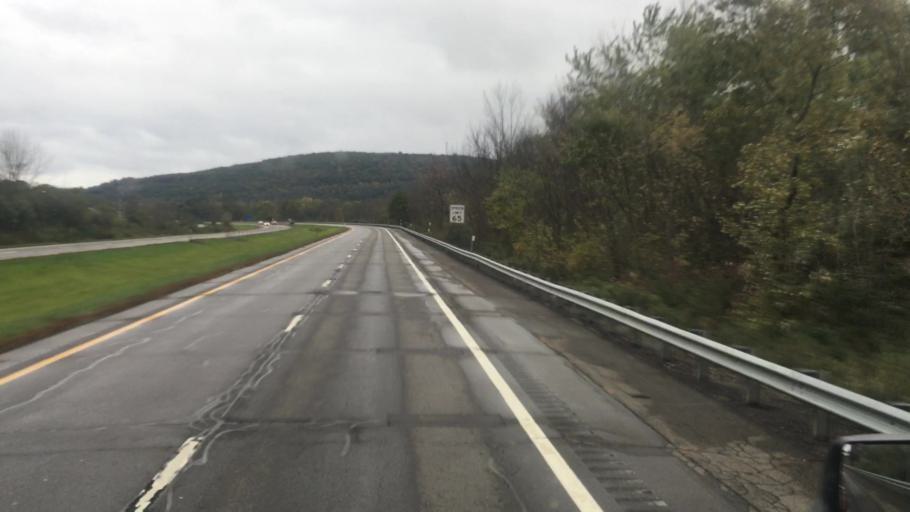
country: US
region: New York
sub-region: Tioga County
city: Owego
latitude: 42.0958
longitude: -76.2365
